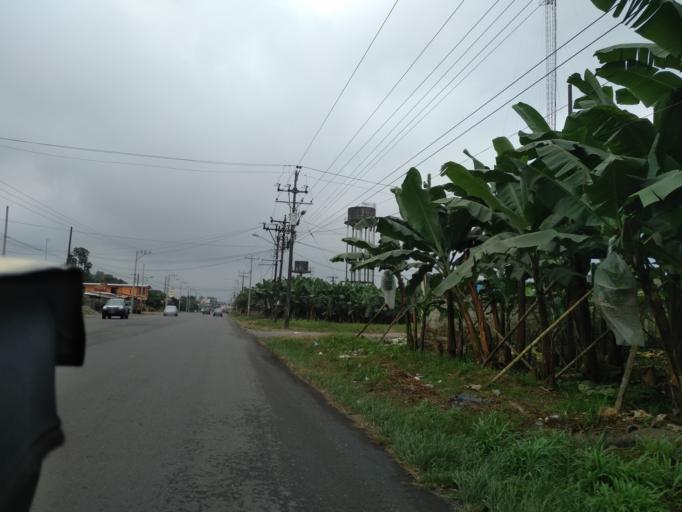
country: EC
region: Cotopaxi
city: La Mana
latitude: -0.9448
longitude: -79.3293
